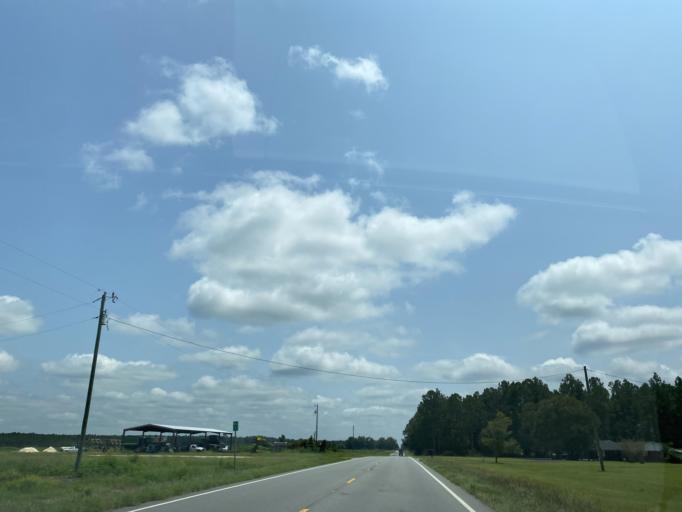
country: US
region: Georgia
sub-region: Jeff Davis County
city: Hazlehurst
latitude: 31.7253
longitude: -82.5288
